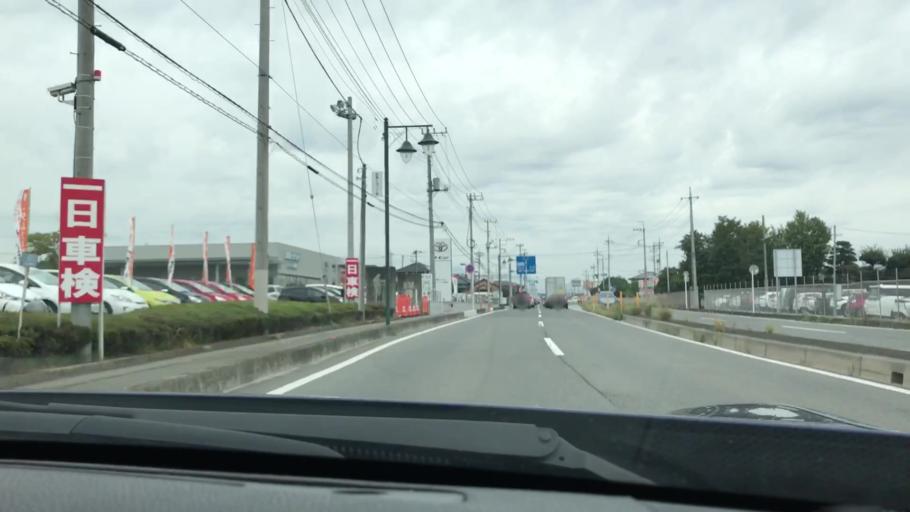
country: JP
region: Gunma
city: Kanekomachi
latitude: 36.3932
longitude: 139.0078
